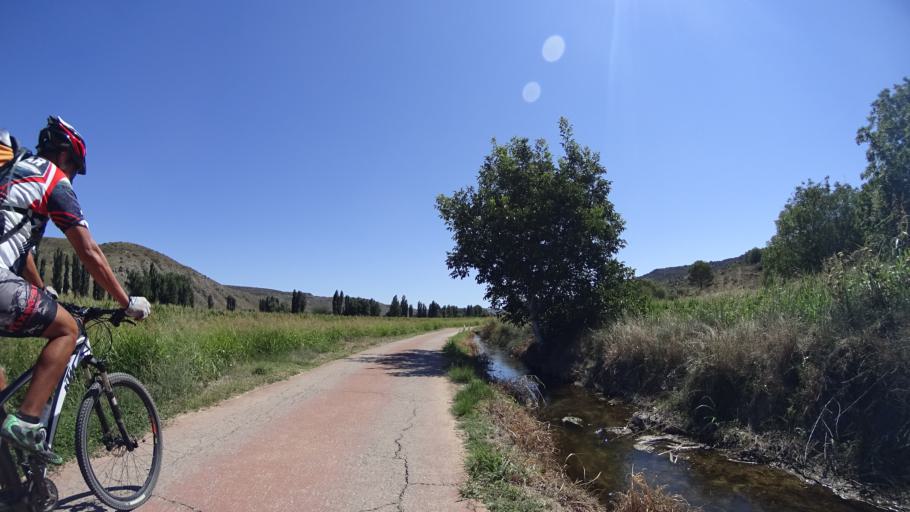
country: ES
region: Madrid
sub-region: Provincia de Madrid
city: Tielmes
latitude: 40.2425
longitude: -3.2920
